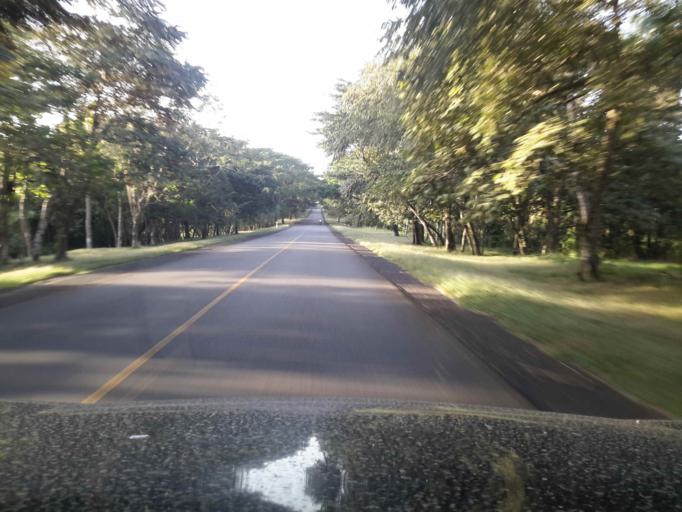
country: NI
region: Rio San Juan
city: San Miguelito
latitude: 11.4048
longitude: -84.8319
